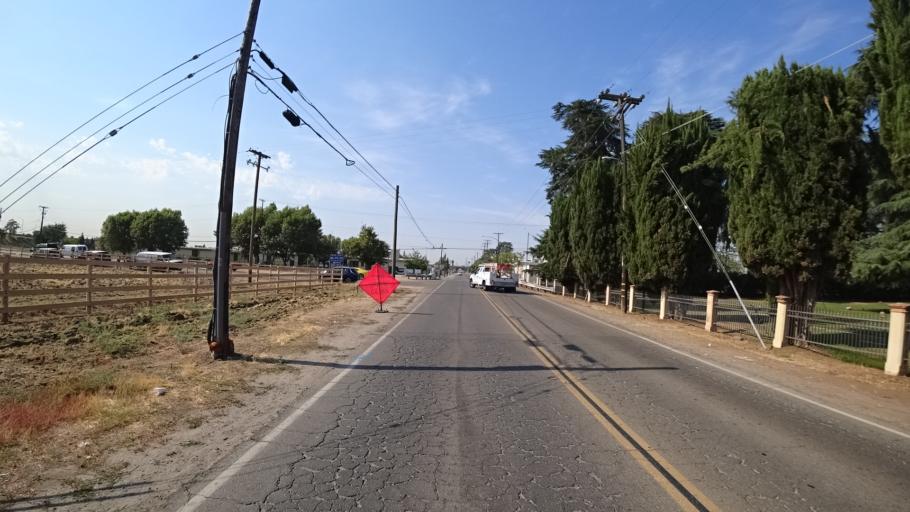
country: US
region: California
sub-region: Fresno County
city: West Park
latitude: 36.7437
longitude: -119.8221
